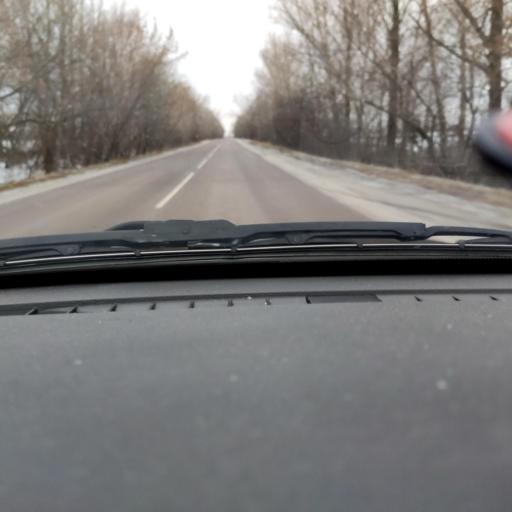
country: RU
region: Voronezj
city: Maslovka
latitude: 51.5304
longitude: 39.3059
